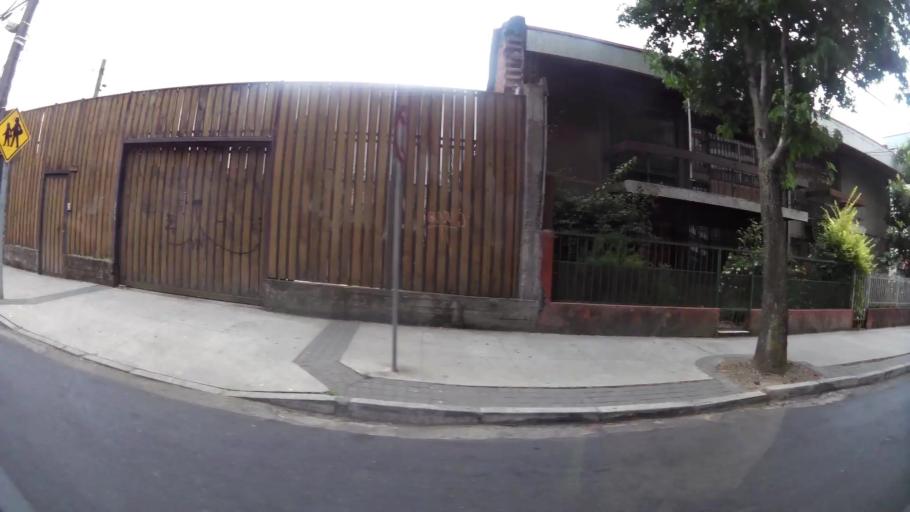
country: CL
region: Biobio
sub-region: Provincia de Concepcion
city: Concepcion
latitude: -36.8217
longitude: -73.0421
